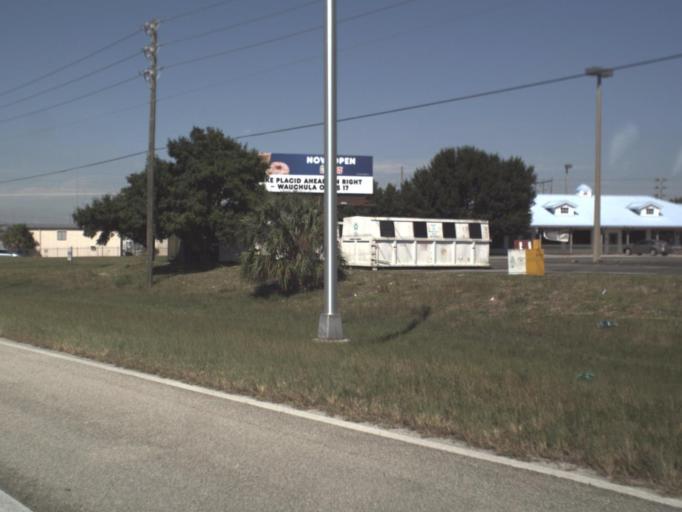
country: US
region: Florida
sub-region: Highlands County
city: Lake Placid
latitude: 27.2657
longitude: -81.3471
